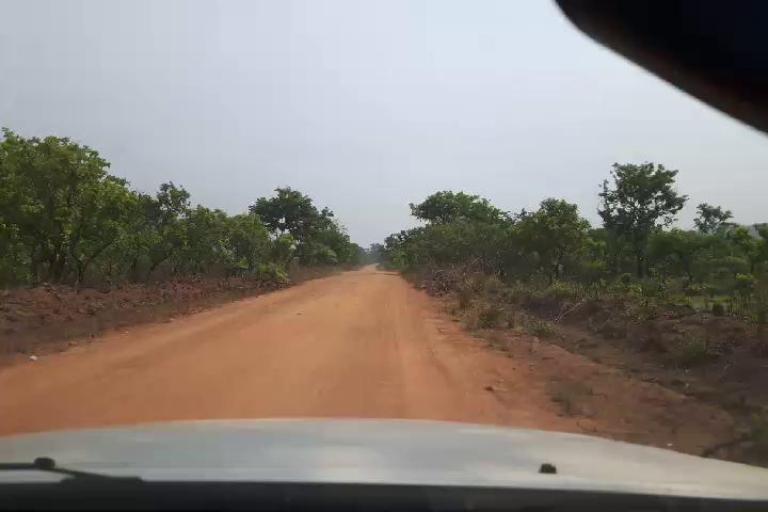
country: SL
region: Northern Province
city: Masingbi
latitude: 8.8881
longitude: -11.8186
